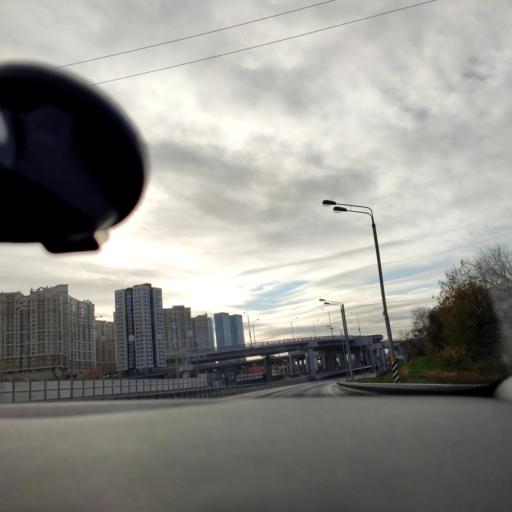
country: RU
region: Moskovskaya
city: Kastanayevo
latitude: 55.7095
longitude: 37.4921
